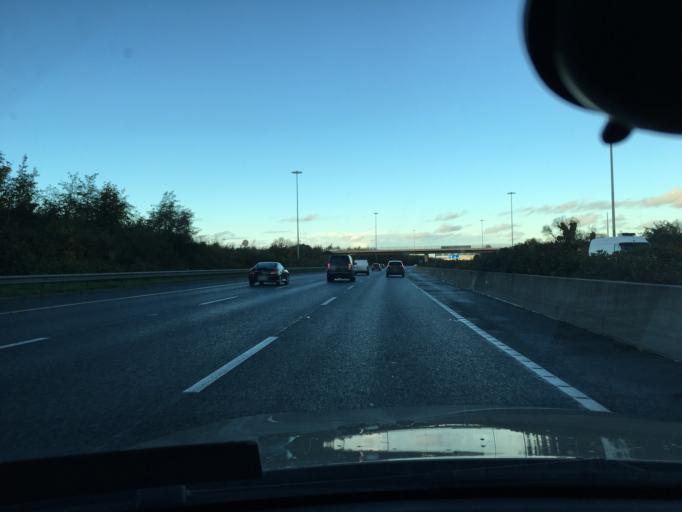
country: IE
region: Leinster
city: Kinsealy-Drinan
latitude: 53.4291
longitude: -6.2166
